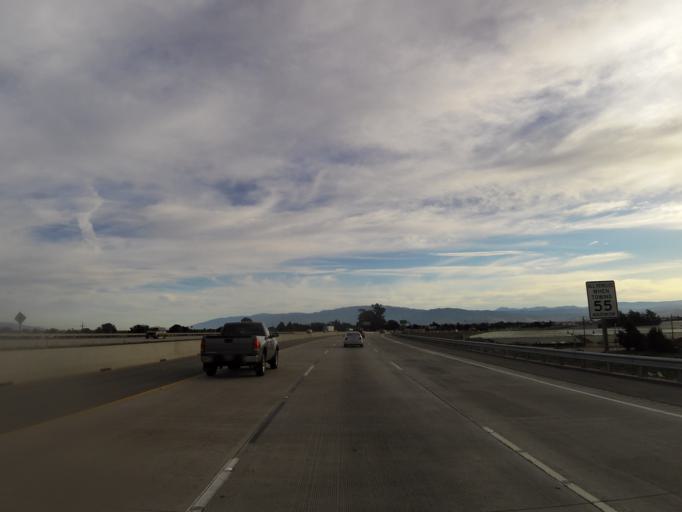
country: US
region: California
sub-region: Monterey County
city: Prunedale
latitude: 36.7371
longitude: -121.6576
